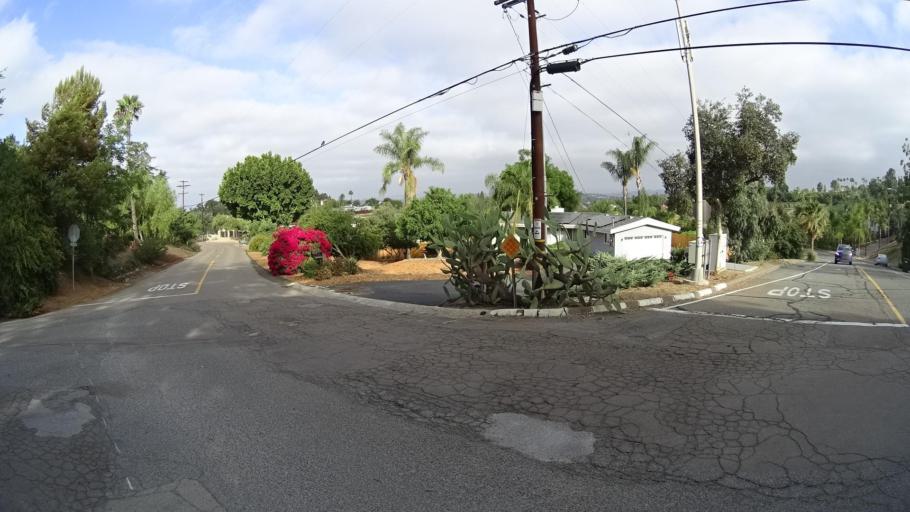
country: US
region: California
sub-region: San Diego County
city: Vista
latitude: 33.1986
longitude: -117.2148
